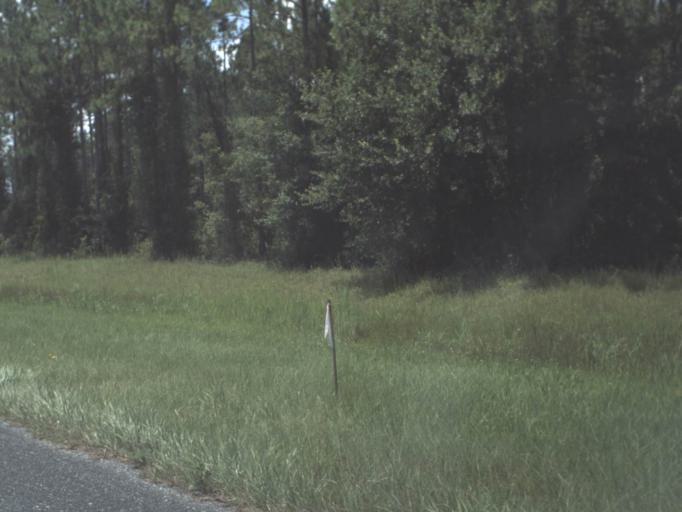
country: US
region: Florida
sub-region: Levy County
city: Bronson
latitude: 29.4569
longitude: -82.6557
